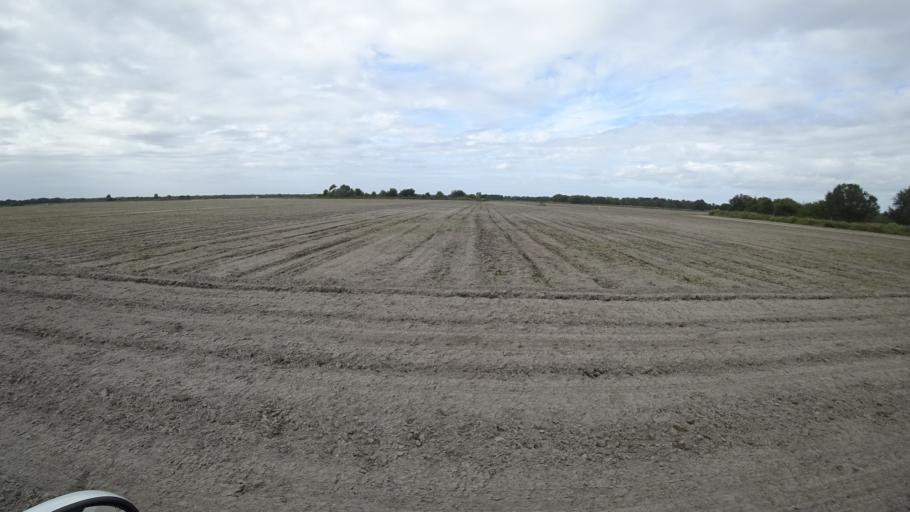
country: US
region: Florida
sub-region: Hillsborough County
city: Wimauma
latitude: 27.5680
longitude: -82.2945
